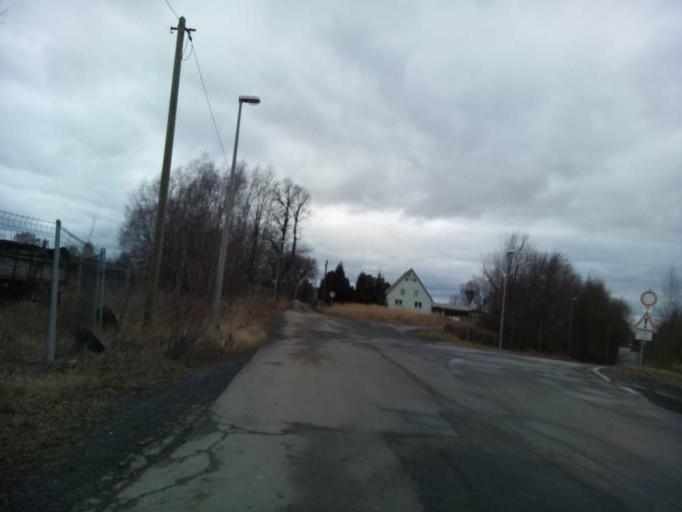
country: DE
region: Saxony
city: Freiberg
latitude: 50.8931
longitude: 13.3297
